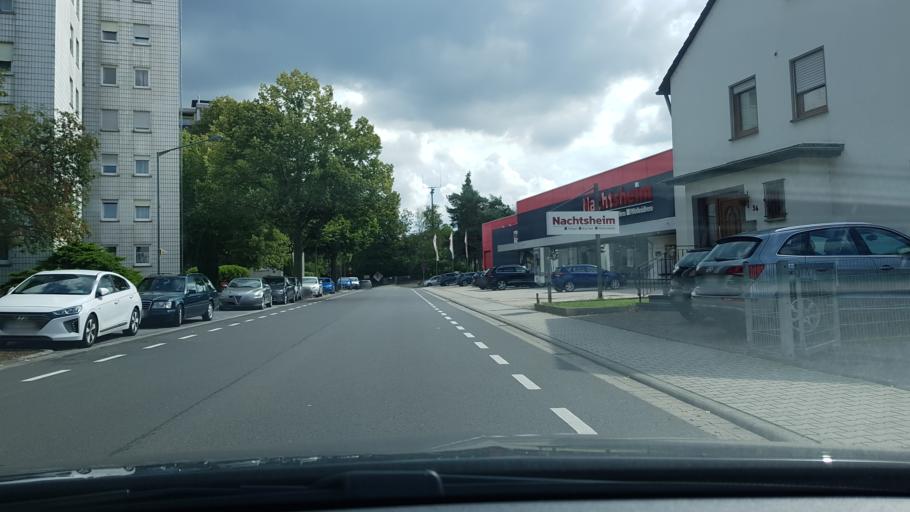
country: DE
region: Rheinland-Pfalz
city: Andernach
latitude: 50.4295
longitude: 7.4164
